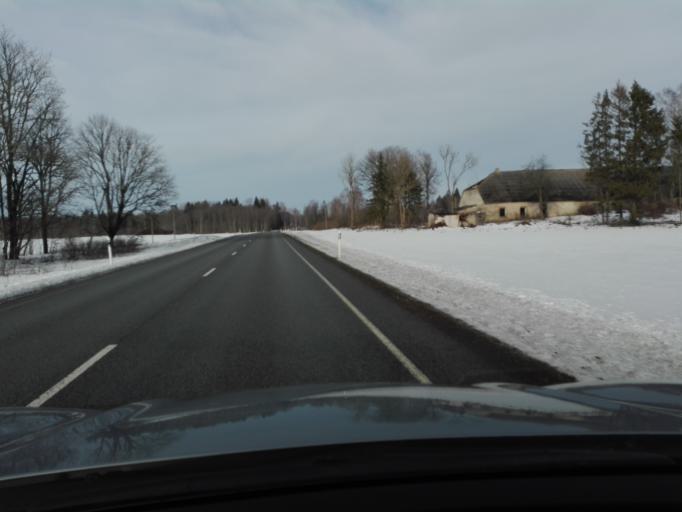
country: EE
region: Raplamaa
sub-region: Rapla vald
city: Rapla
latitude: 58.9198
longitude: 24.7554
